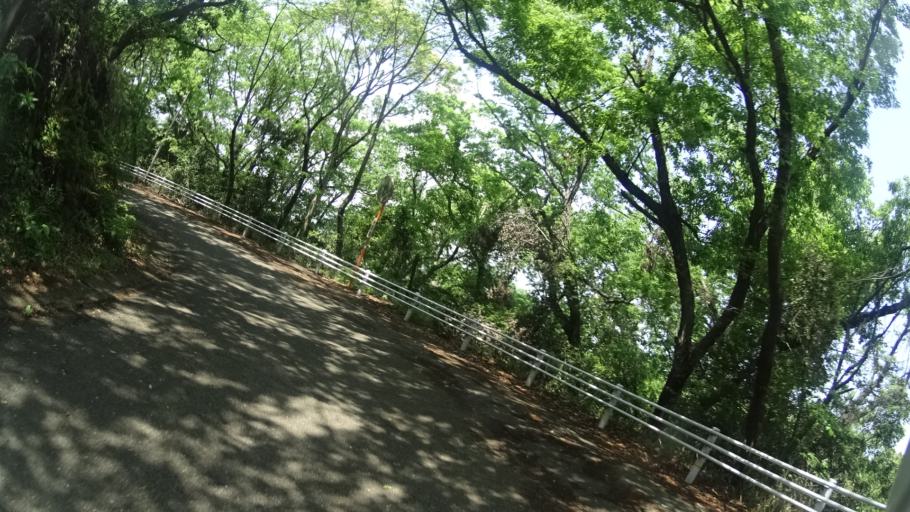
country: JP
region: Tokushima
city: Tokushima-shi
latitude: 34.0677
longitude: 134.5182
